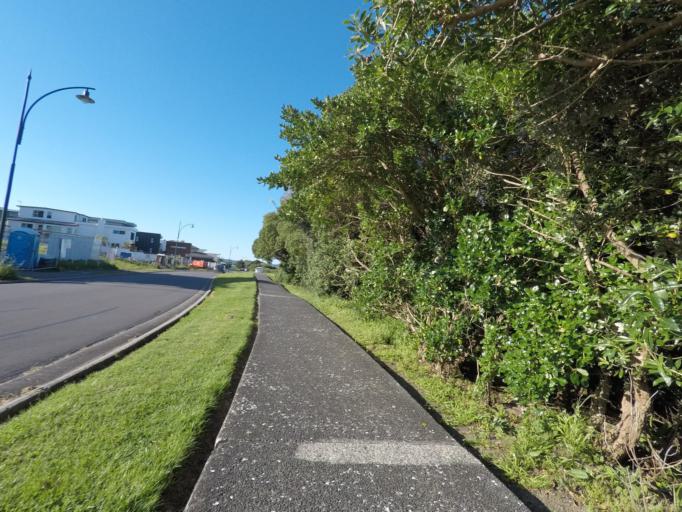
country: NZ
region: Auckland
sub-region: Auckland
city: Rosebank
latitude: -36.8359
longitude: 174.6617
